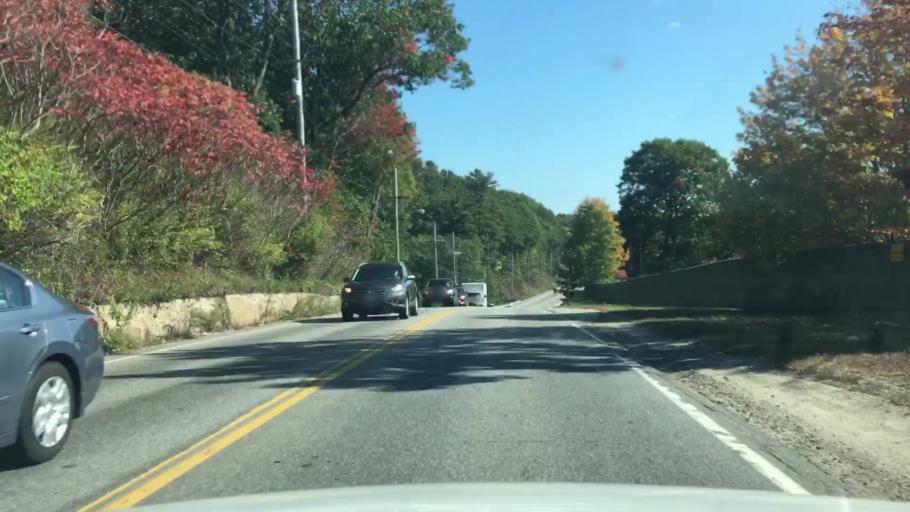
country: US
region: Maine
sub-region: Androscoggin County
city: Lisbon Falls
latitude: 43.9936
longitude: -70.0535
